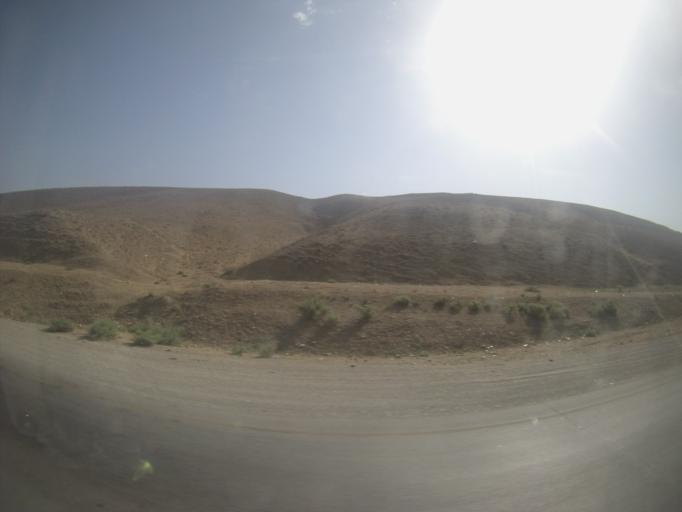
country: AZ
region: Qobustan
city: Qobustan
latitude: 40.4996
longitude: 49.0381
